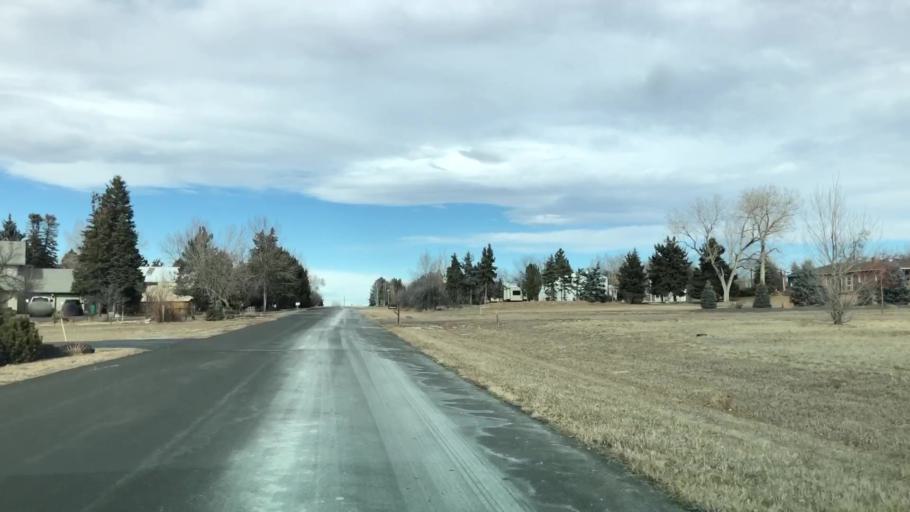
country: US
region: Colorado
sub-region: Weld County
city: Windsor
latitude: 40.5333
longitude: -104.9346
